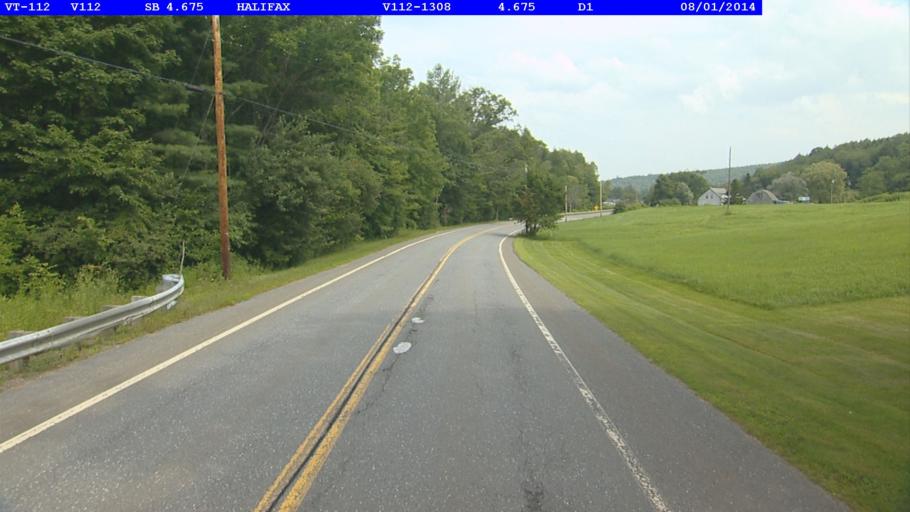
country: US
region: Massachusetts
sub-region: Franklin County
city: Colrain
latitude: 42.7652
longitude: -72.7933
